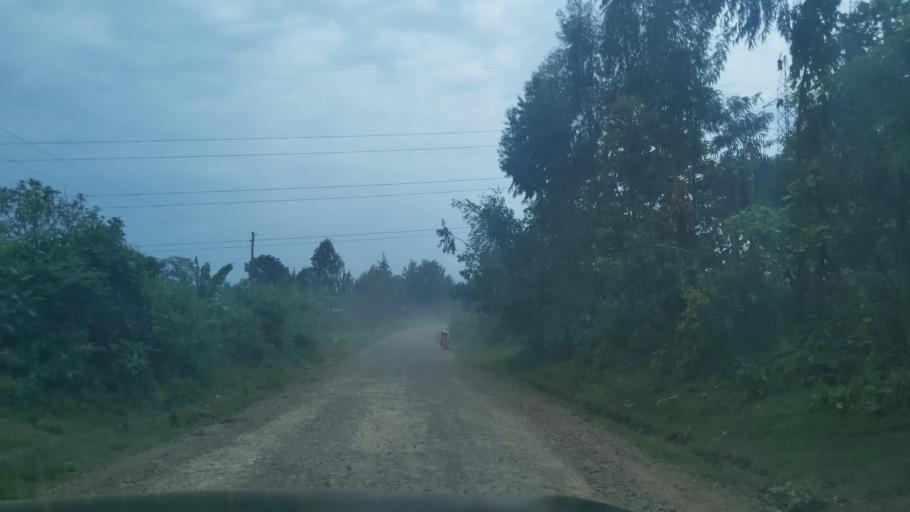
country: ET
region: Oromiya
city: Jima
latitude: 7.7364
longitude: 36.7703
